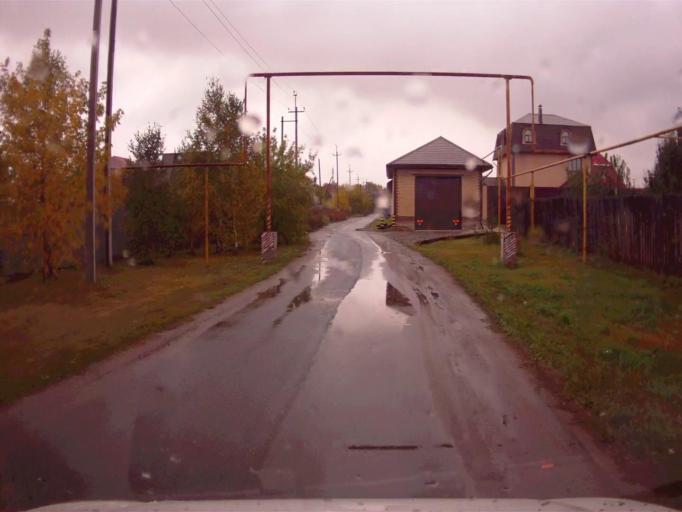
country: RU
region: Chelyabinsk
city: Dolgoderevenskoye
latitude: 55.3051
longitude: 61.3414
